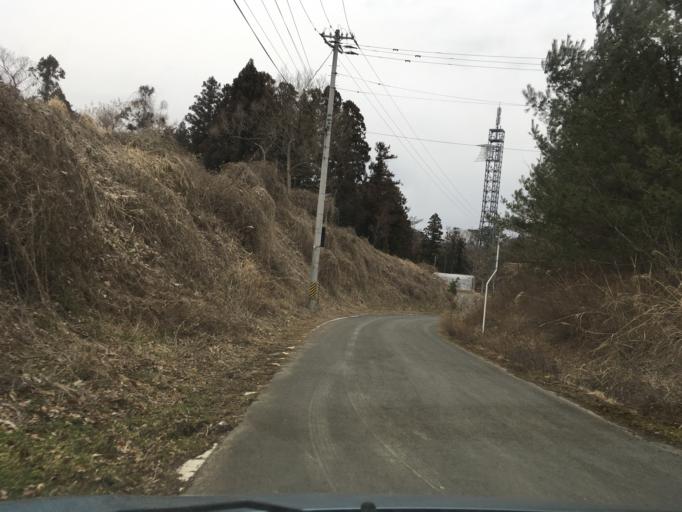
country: JP
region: Miyagi
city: Wakuya
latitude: 38.6616
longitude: 141.2813
